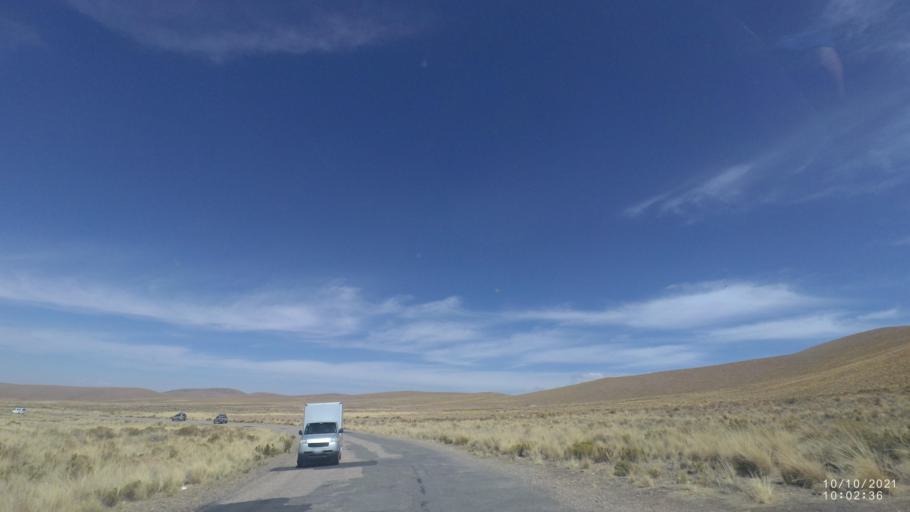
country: BO
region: La Paz
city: Eucaliptus
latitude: -17.3596
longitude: -67.4352
